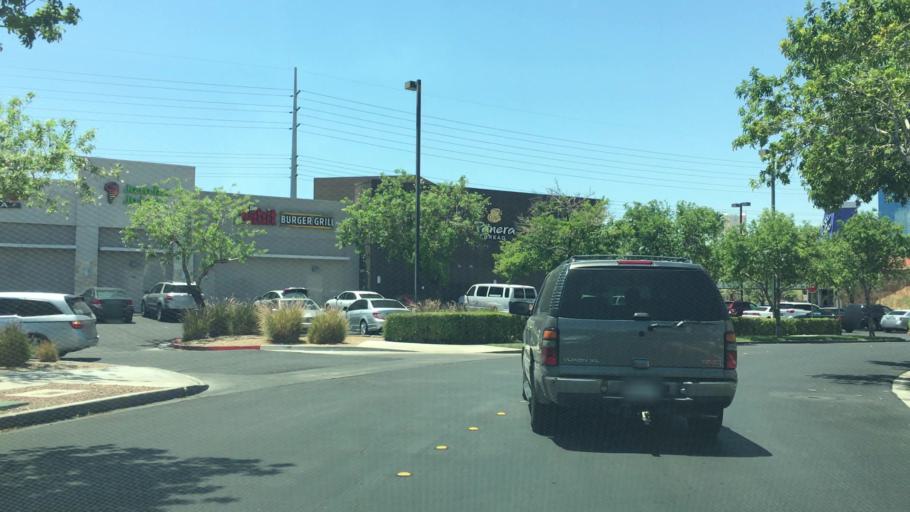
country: US
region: Nevada
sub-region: Clark County
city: Paradise
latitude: 36.1155
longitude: -115.1554
